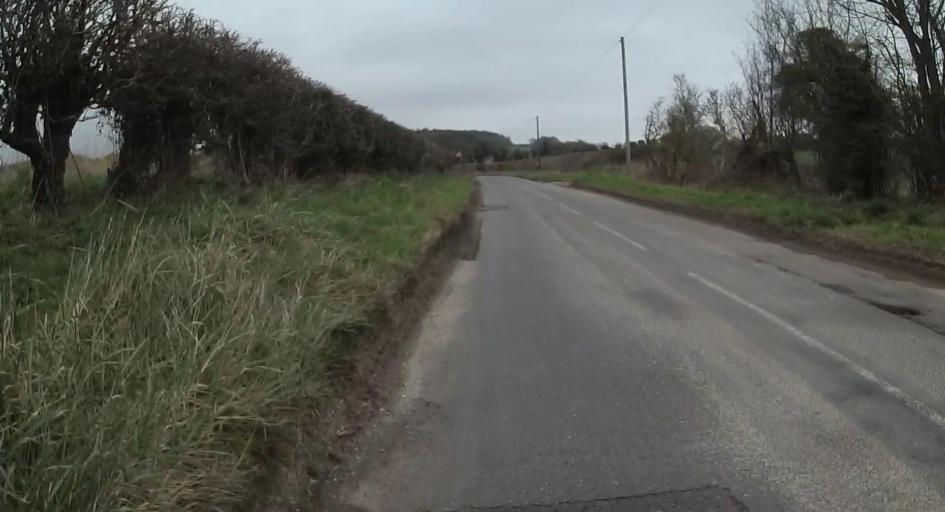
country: GB
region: England
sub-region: Hampshire
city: Basingstoke
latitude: 51.1892
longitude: -1.1202
